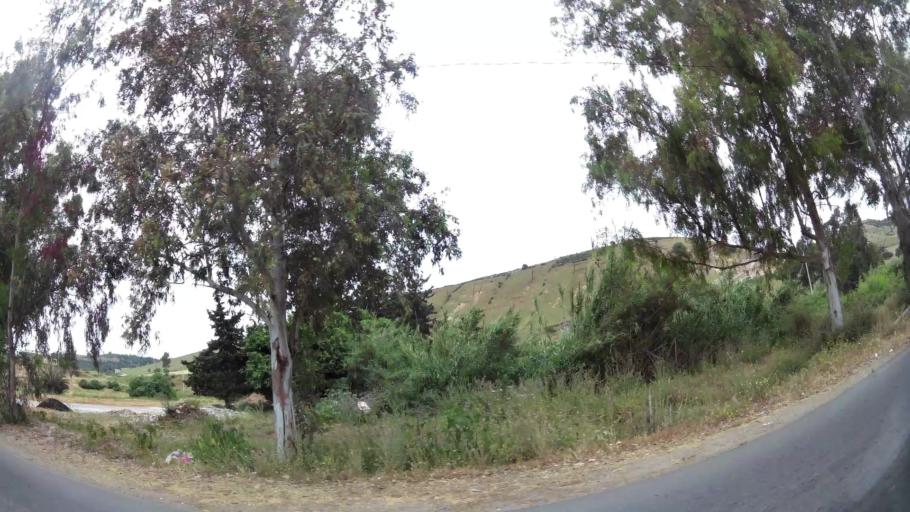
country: MA
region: Rabat-Sale-Zemmour-Zaer
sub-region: Rabat
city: Rabat
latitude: 33.9846
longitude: -6.7621
